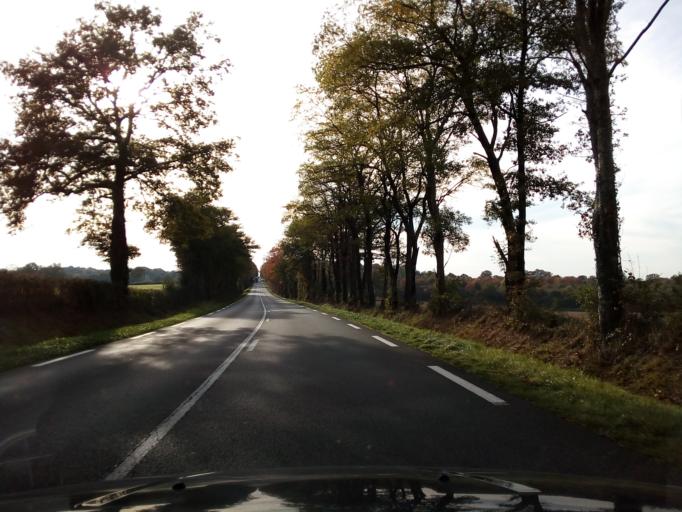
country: FR
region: Poitou-Charentes
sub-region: Departement de la Charente
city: Confolens
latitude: 46.0695
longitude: 0.7225
